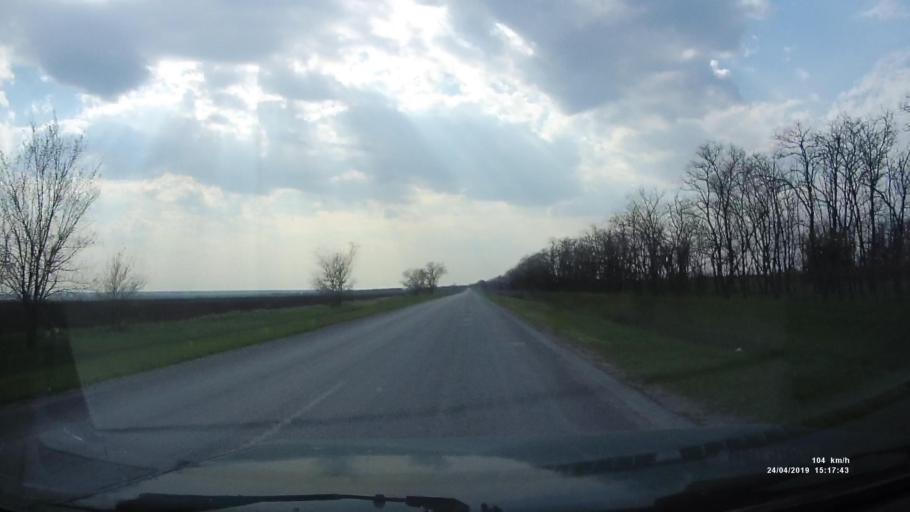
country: RU
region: Rostov
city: Remontnoye
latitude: 46.5465
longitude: 43.1833
